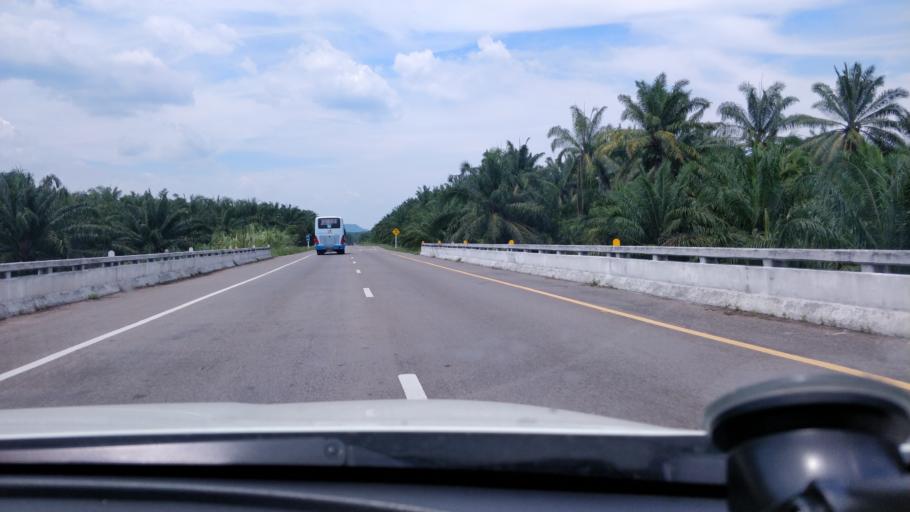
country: TH
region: Krabi
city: Plai Phraya
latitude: 8.5336
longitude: 98.9017
